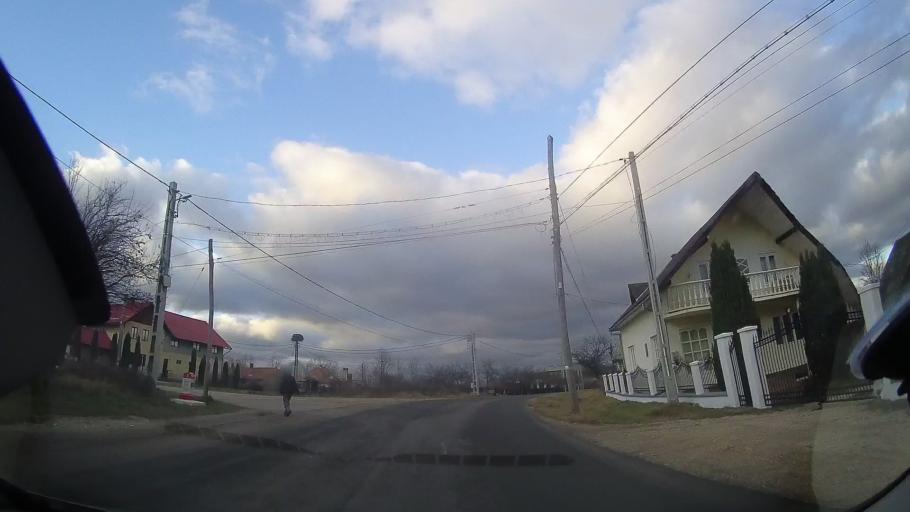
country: RO
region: Cluj
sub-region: Comuna Calatele
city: Calatele
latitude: 46.7746
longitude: 23.0069
